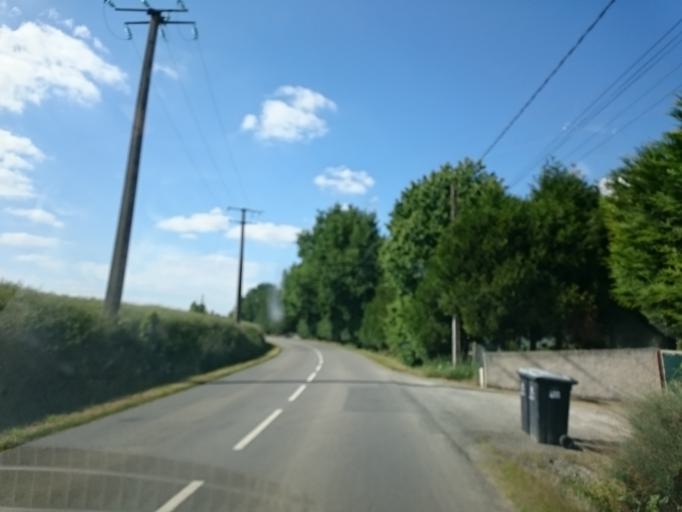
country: FR
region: Brittany
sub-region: Departement d'Ille-et-Vilaine
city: Chanteloup
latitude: 47.9398
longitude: -1.6037
